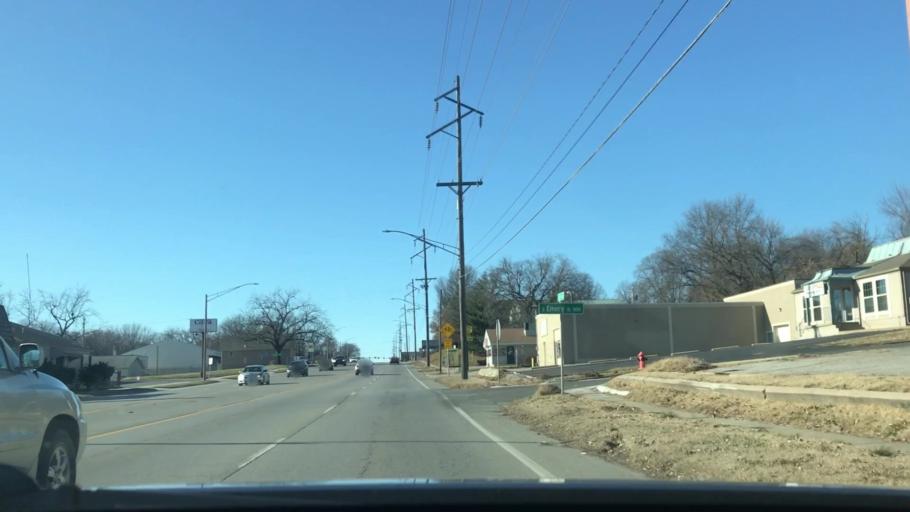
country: US
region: Missouri
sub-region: Jackson County
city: Independence
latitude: 39.0790
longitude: -94.4078
